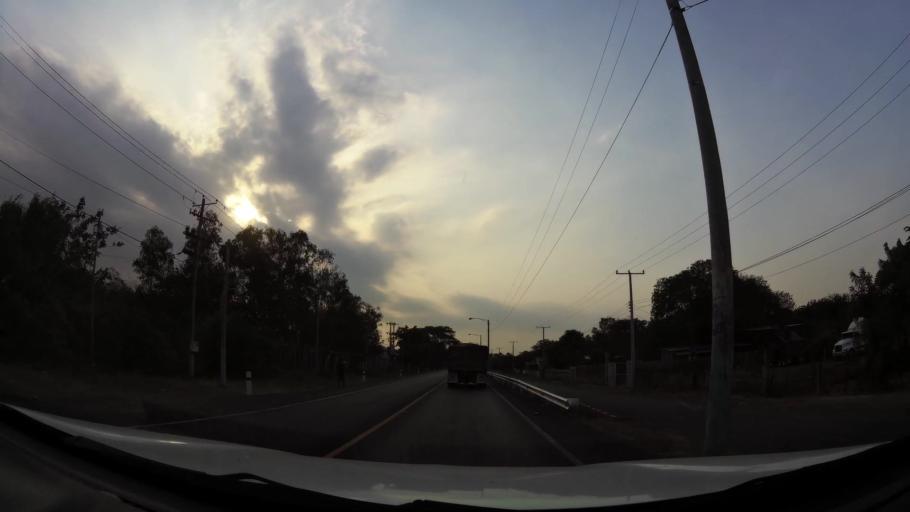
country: NI
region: Managua
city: Ciudad Sandino
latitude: 12.1845
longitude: -86.3605
